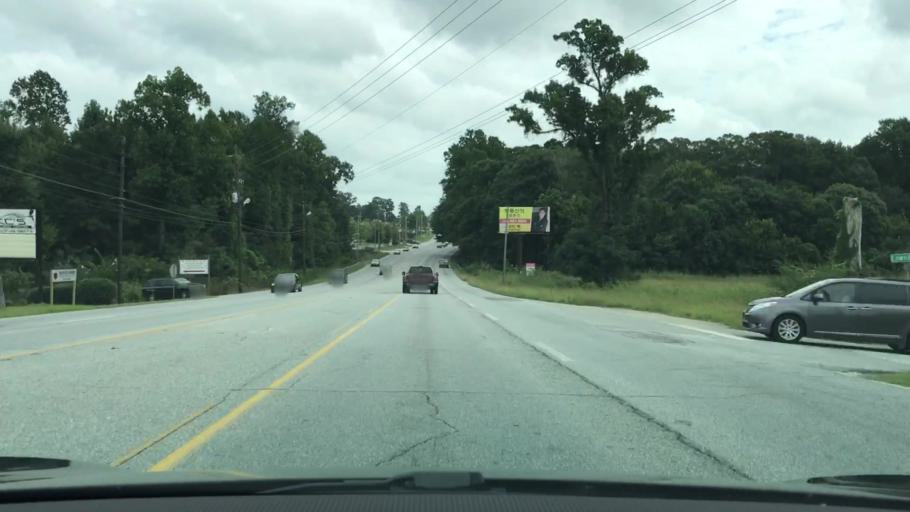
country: US
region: Alabama
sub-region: Lee County
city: Opelika
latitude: 32.6343
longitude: -85.4271
